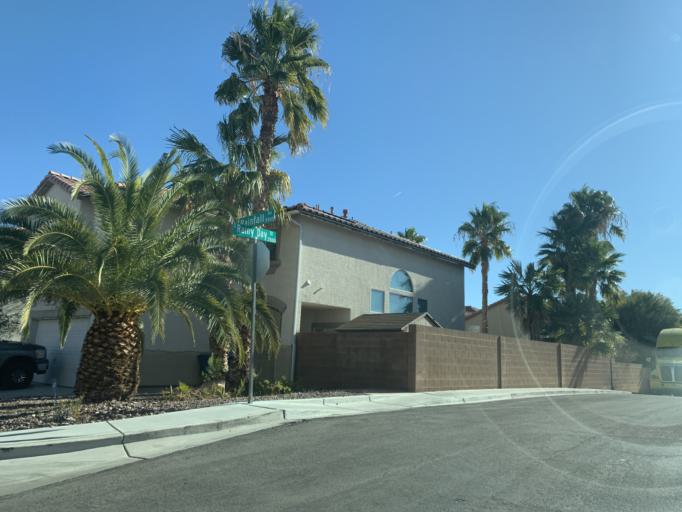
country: US
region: Nevada
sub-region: Clark County
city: Summerlin South
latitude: 36.1257
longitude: -115.3004
